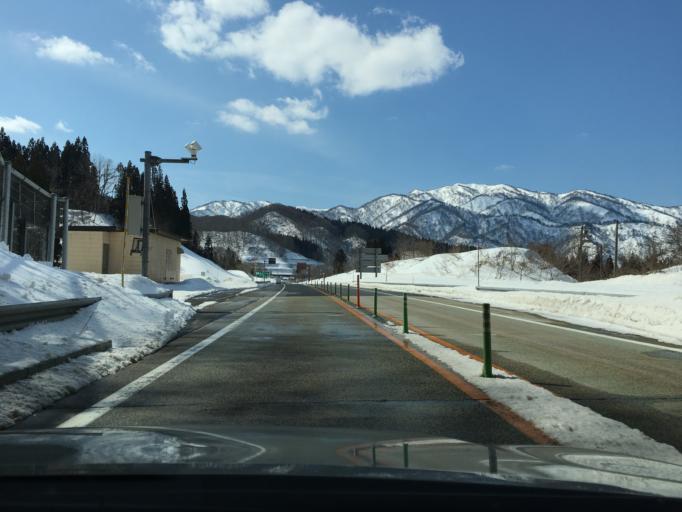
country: JP
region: Yamagata
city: Sagae
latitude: 38.4460
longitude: 140.0192
